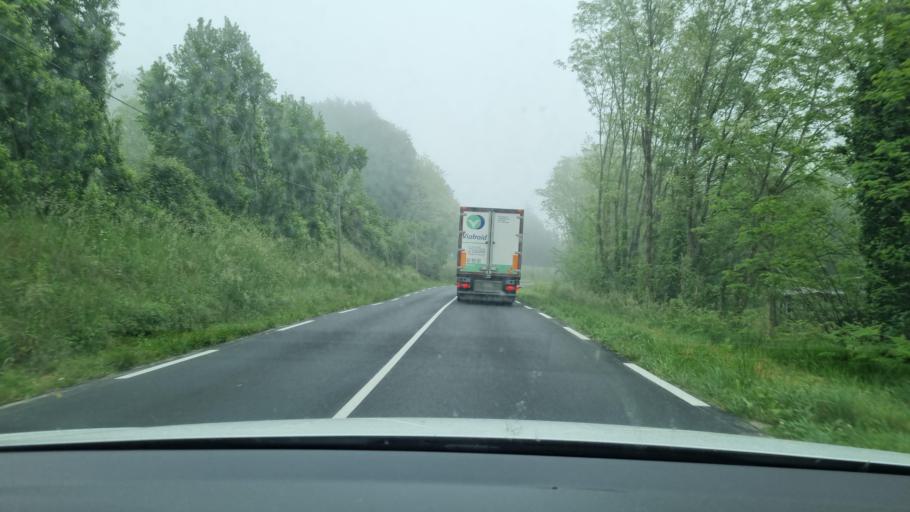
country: FR
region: Aquitaine
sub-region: Departement des Pyrenees-Atlantiques
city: Orthez
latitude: 43.5222
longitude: -0.7110
